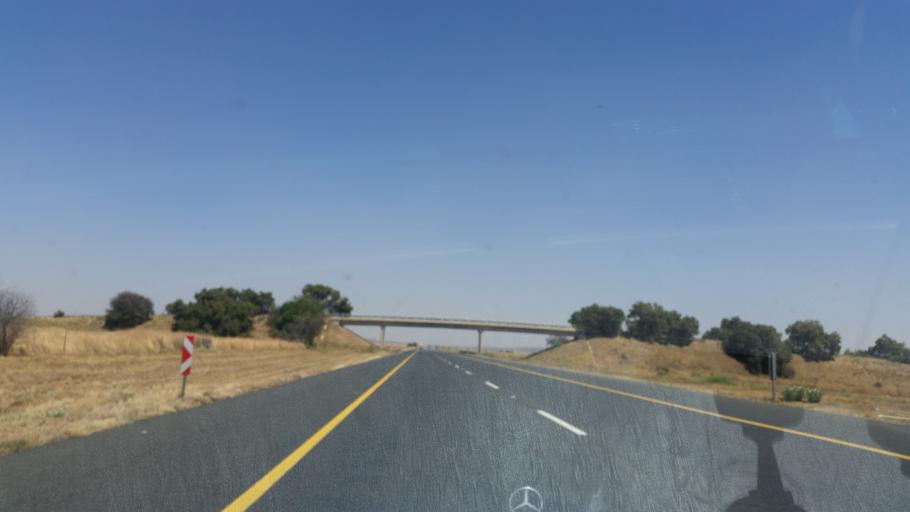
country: ZA
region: Orange Free State
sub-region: Lejweleputswa District Municipality
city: Winburg
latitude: -28.6531
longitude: 26.8718
